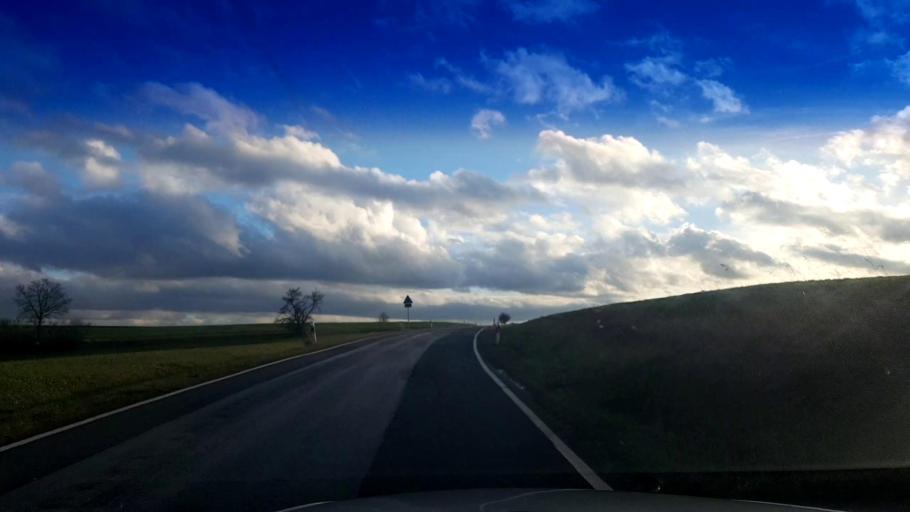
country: DE
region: Bavaria
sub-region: Upper Franconia
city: Buttenheim
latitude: 49.8205
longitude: 11.0255
